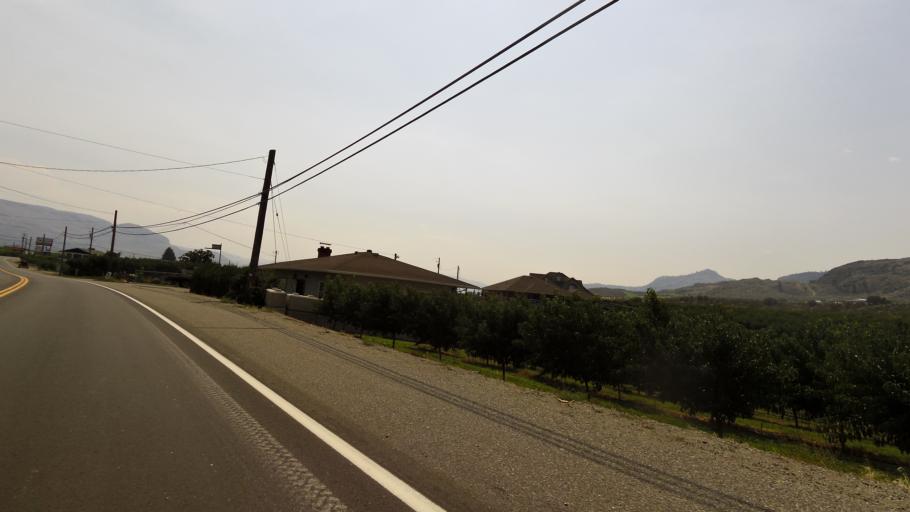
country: CA
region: British Columbia
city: Osoyoos
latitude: 49.0428
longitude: -119.4886
